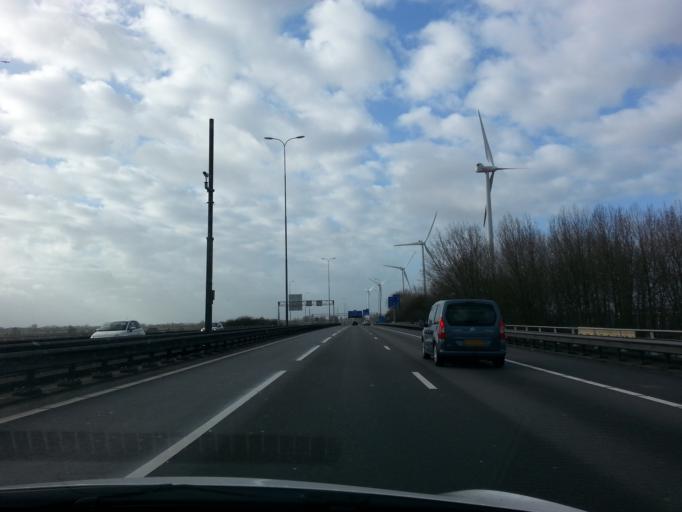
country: NL
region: Utrecht
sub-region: Gemeente Utrecht
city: Lunetten
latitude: 52.0255
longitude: 5.1309
